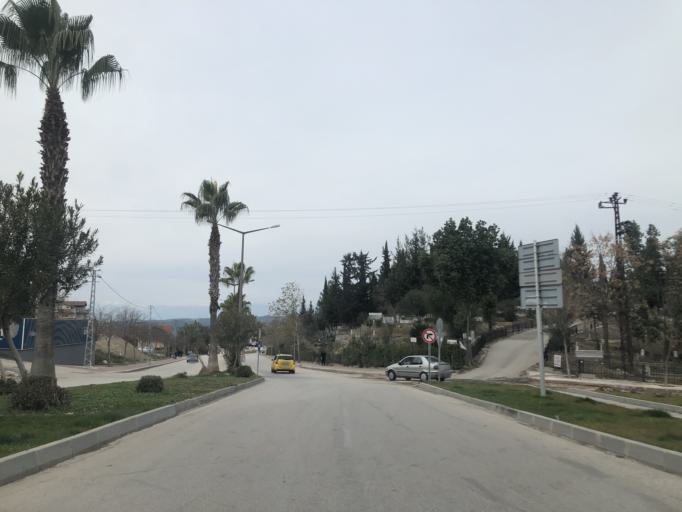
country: TR
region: Adana
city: Adana
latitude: 37.0533
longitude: 35.2971
